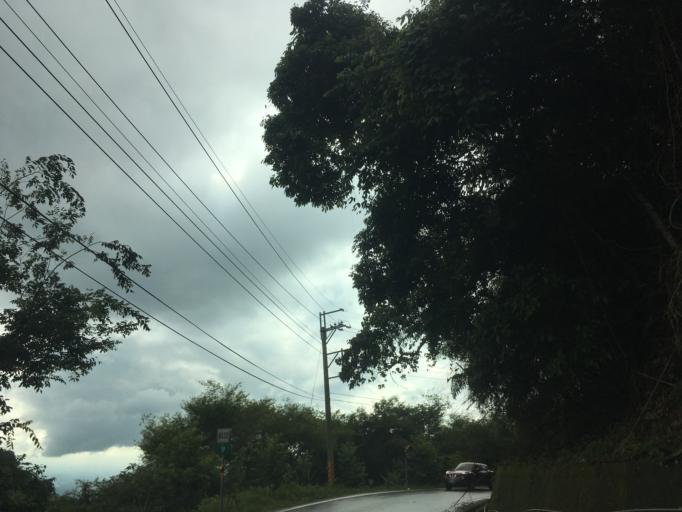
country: TW
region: Taiwan
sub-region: Chiayi
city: Jiayi Shi
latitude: 23.4444
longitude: 120.6694
